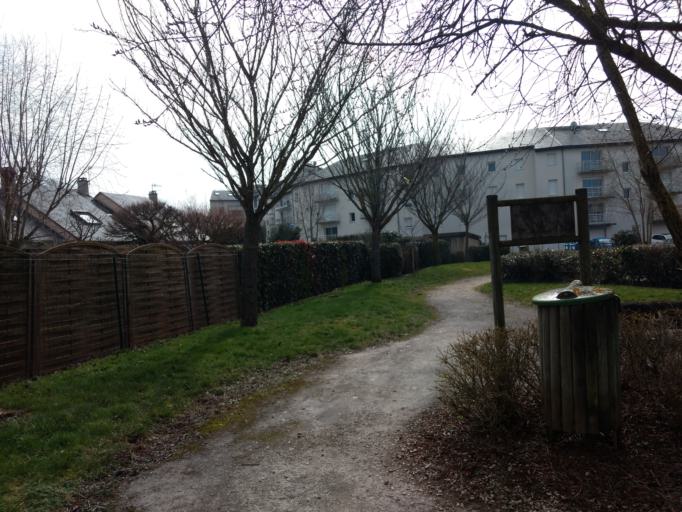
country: FR
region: Midi-Pyrenees
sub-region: Departement de l'Aveyron
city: Rodez
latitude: 44.3682
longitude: 2.5855
